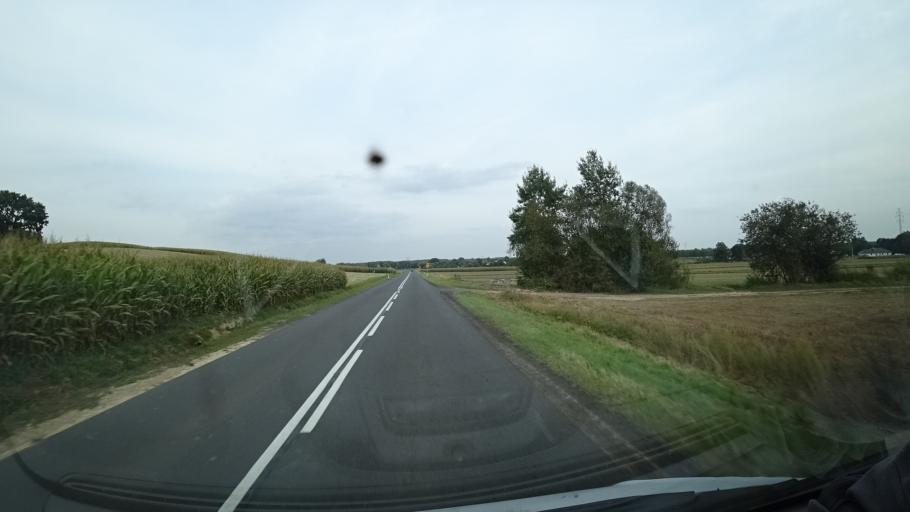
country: PL
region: Silesian Voivodeship
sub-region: Powiat gliwicki
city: Toszek
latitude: 50.3976
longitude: 18.4727
